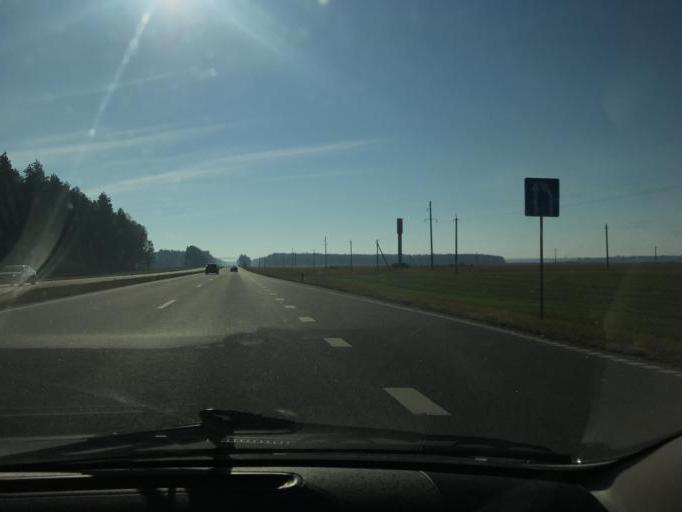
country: BY
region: Minsk
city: Slutsk
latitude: 53.3228
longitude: 27.5335
